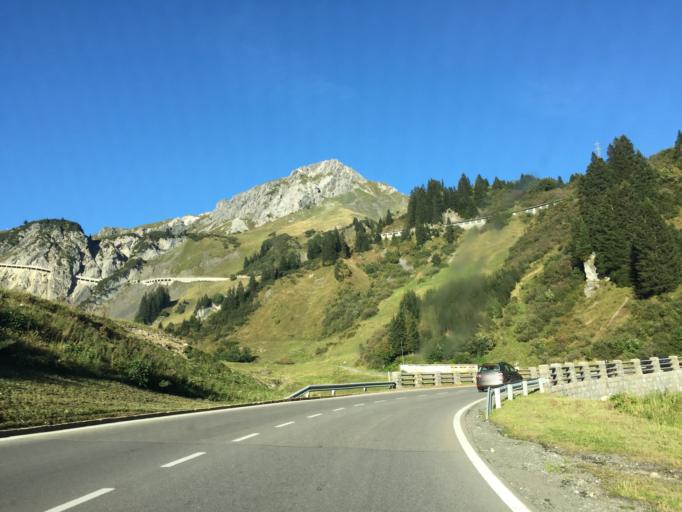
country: AT
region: Vorarlberg
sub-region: Politischer Bezirk Bludenz
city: Lech
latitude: 47.1409
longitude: 10.1605
